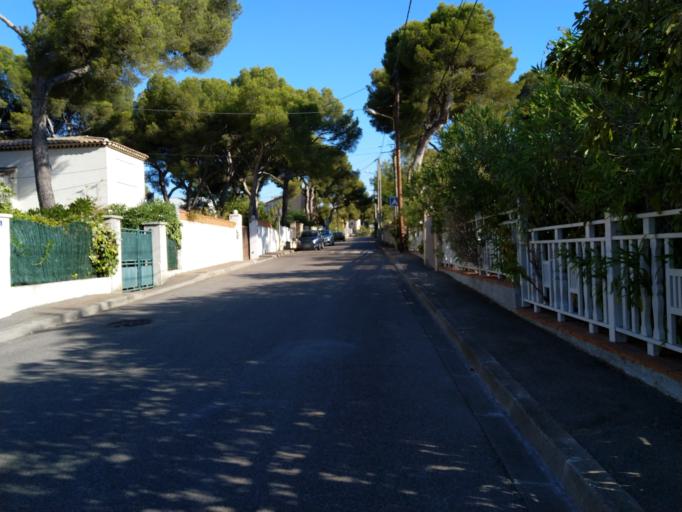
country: FR
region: Provence-Alpes-Cote d'Azur
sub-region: Departement des Bouches-du-Rhone
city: Sausset-les-Pins
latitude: 43.3324
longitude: 5.1217
